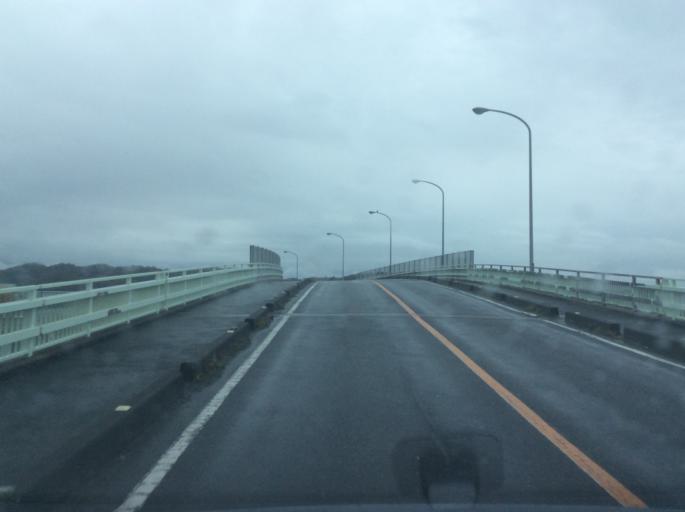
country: JP
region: Fukushima
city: Iwaki
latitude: 37.0773
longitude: 140.9532
